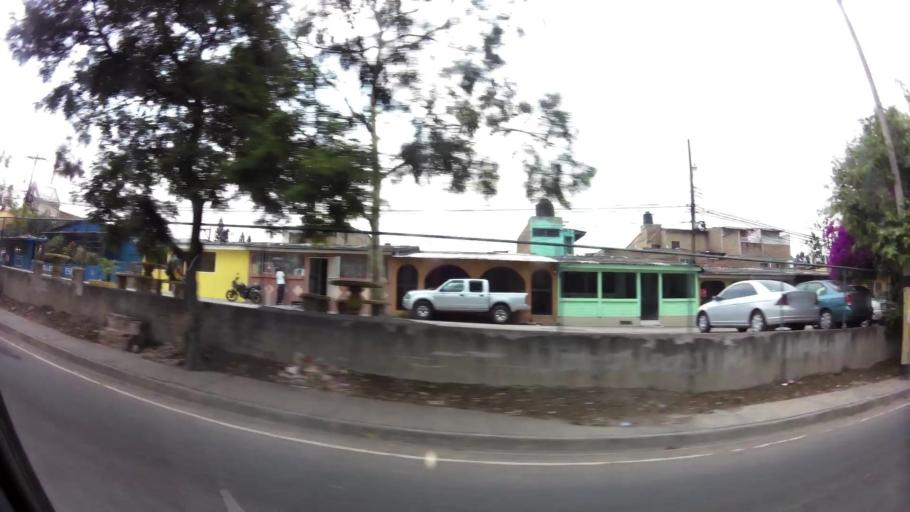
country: HN
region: Francisco Morazan
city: El Tablon
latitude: 14.0668
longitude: -87.1732
